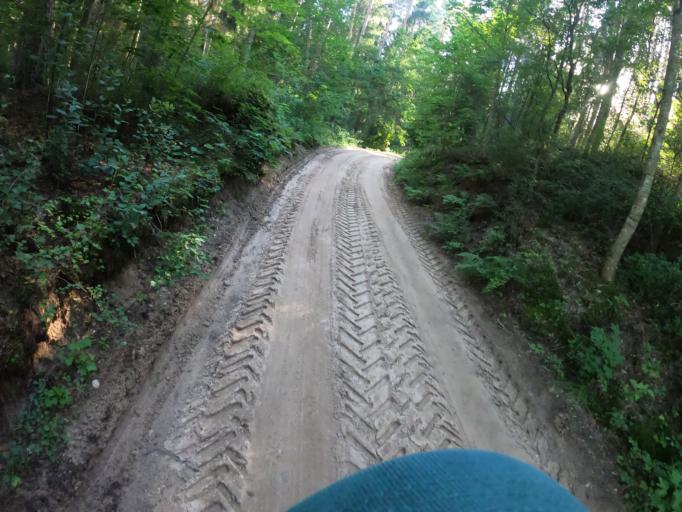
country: LT
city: Kursenai
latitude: 55.8146
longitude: 22.9200
